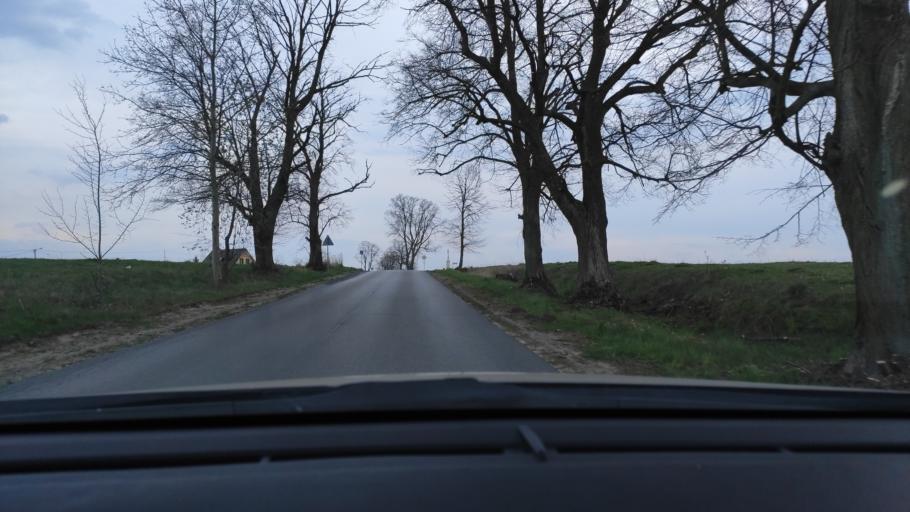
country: PL
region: Masovian Voivodeship
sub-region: Powiat kozienicki
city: Ryczywol
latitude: 51.5941
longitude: 21.3514
